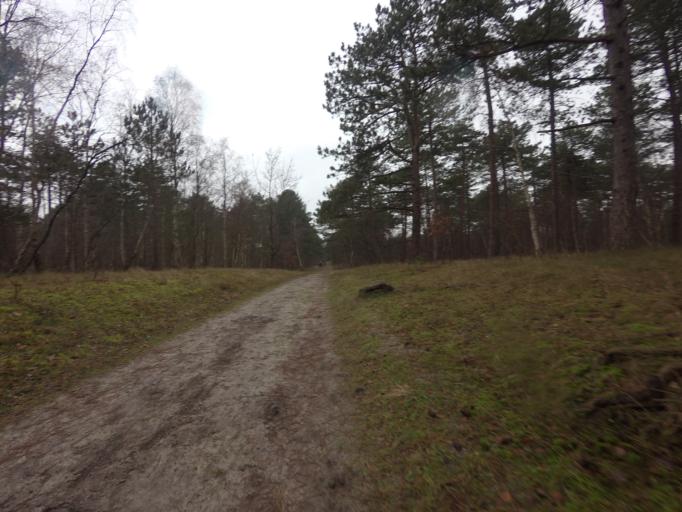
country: NL
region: Zeeland
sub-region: Schouwen-Duiveland
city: Burgh
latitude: 51.6830
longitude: 3.7057
